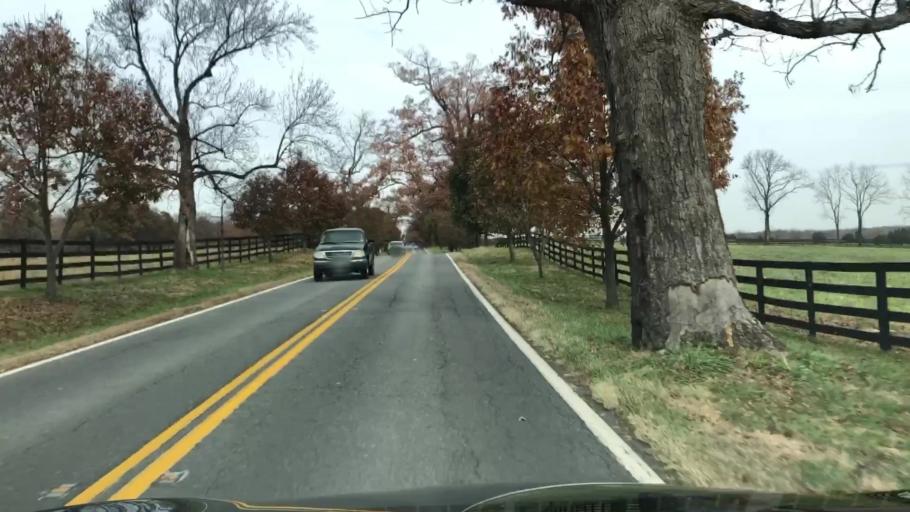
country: US
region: Virginia
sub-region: Fauquier County
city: New Baltimore
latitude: 38.7696
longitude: -77.6811
